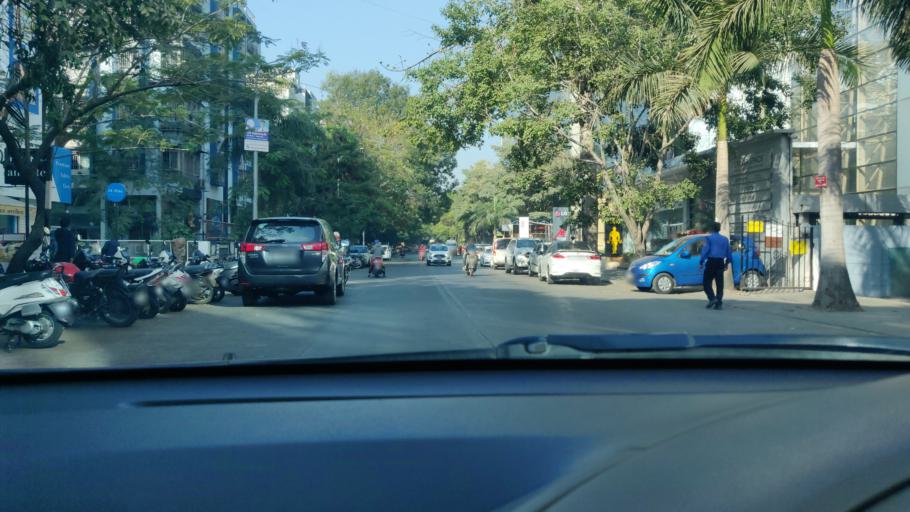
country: IN
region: Maharashtra
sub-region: Pune Division
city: Khadki
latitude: 18.5534
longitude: 73.8080
